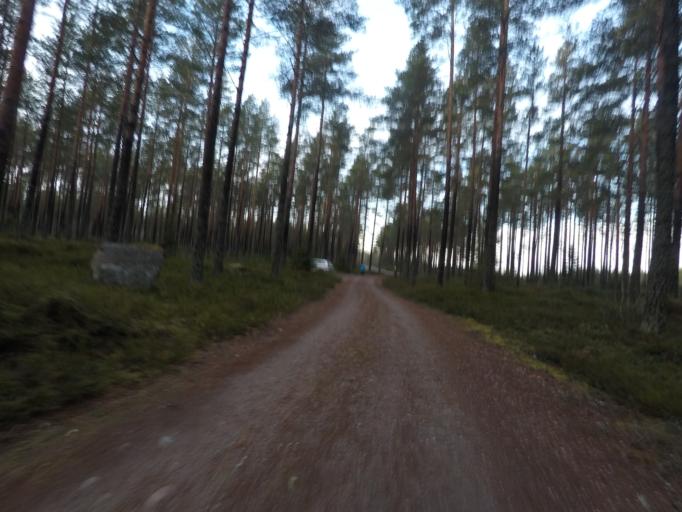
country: SE
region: Vaestmanland
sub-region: Kungsors Kommun
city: Kungsoer
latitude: 59.3635
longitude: 16.1184
